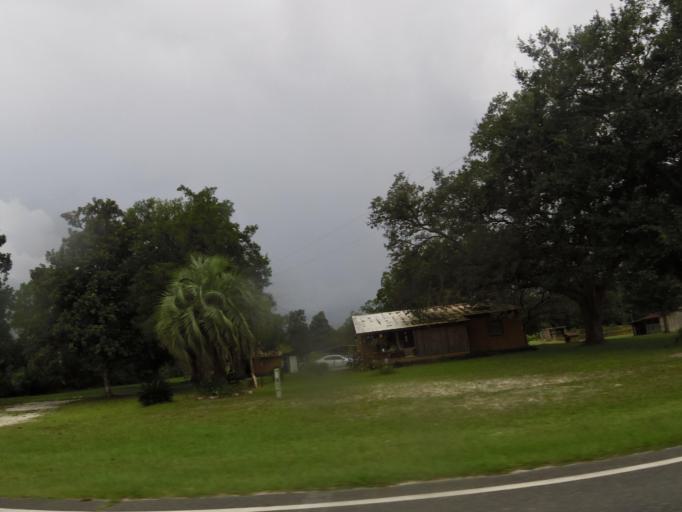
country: US
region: Florida
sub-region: Baker County
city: Macclenny
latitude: 30.4149
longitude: -82.1972
